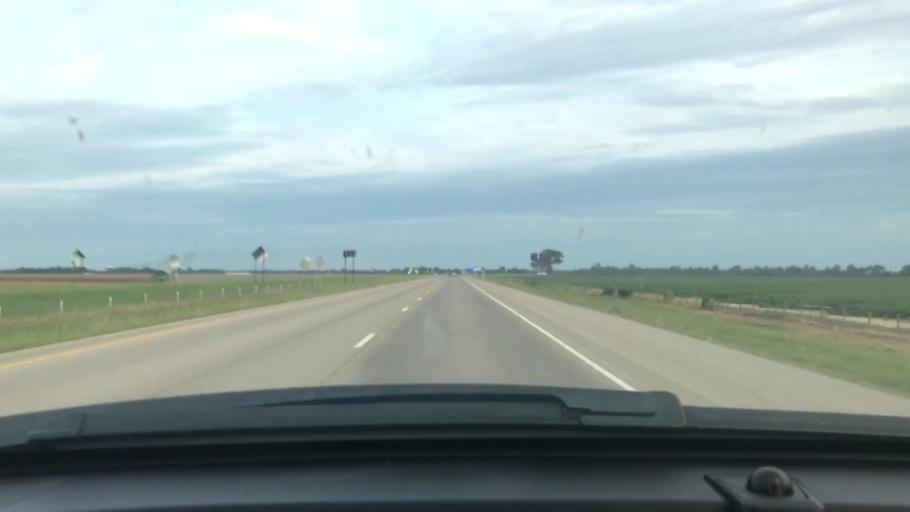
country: US
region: Arkansas
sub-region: Craighead County
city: Bay
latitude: 35.7048
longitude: -90.5656
